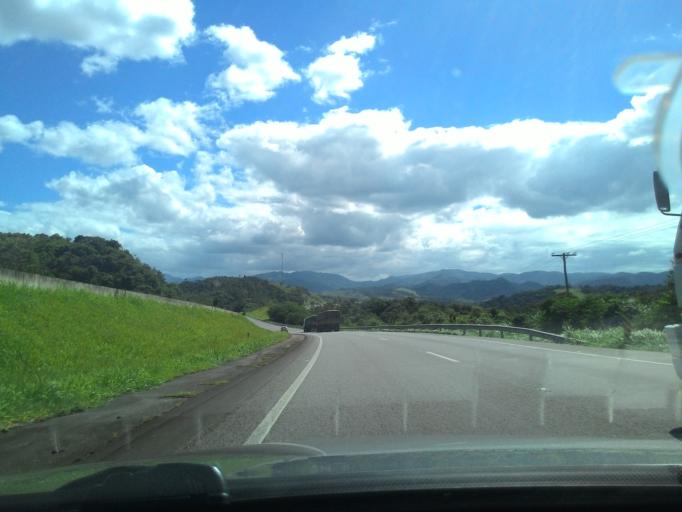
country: BR
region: Sao Paulo
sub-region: Cajati
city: Cajati
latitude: -24.7458
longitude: -48.1474
